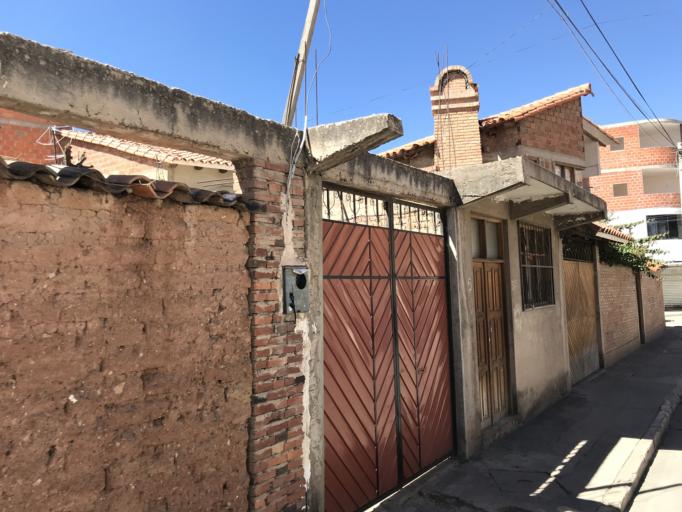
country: BO
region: Chuquisaca
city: Sucre
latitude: -19.0377
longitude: -65.2528
